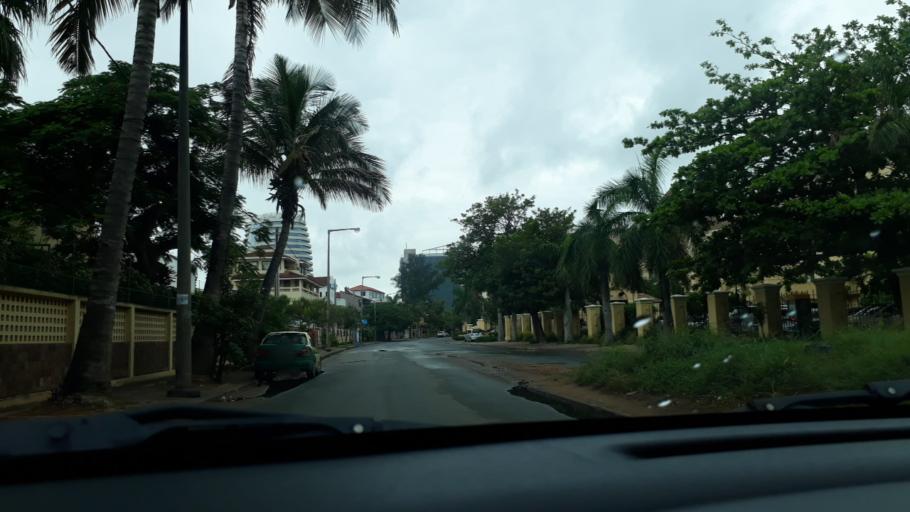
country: MZ
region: Maputo City
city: Maputo
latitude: -25.9610
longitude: 32.6039
